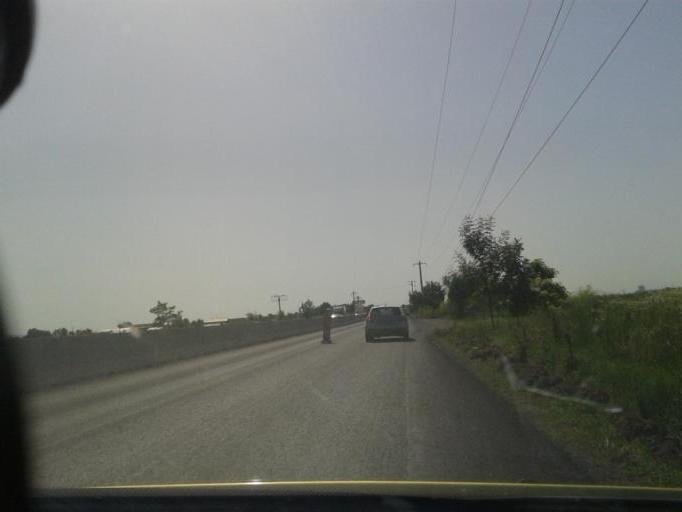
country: RO
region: Prahova
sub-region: Comuna Paulesti
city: Paulesti
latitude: 44.9760
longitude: 25.9447
